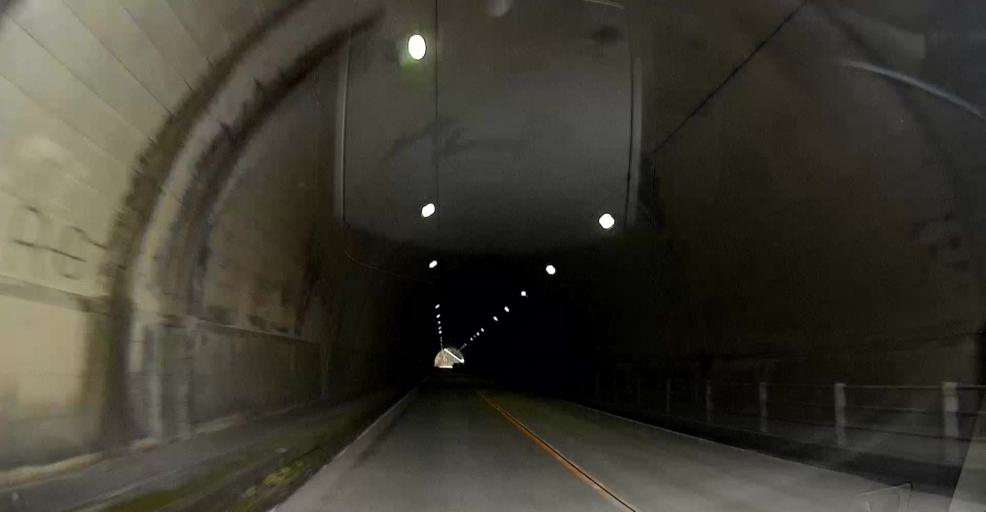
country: JP
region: Kumamoto
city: Matsubase
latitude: 32.6174
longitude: 130.8544
